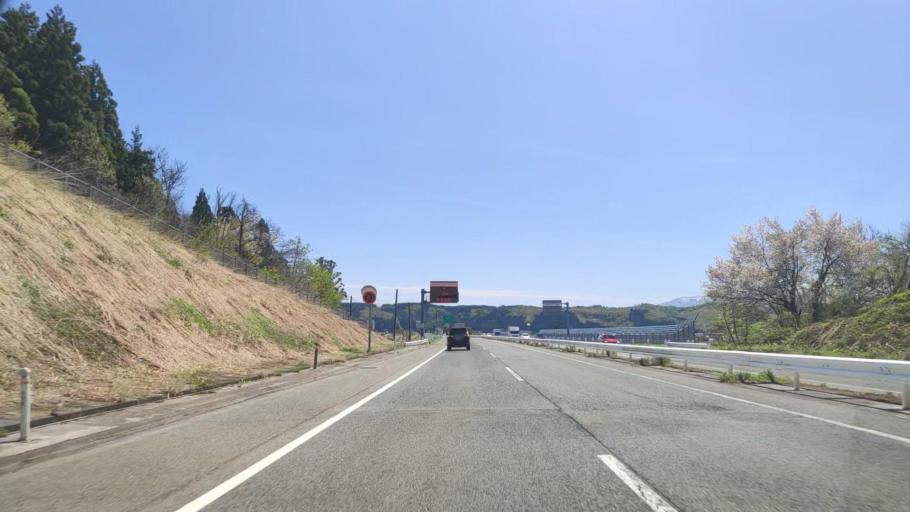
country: JP
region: Yamagata
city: Shinjo
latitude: 38.7091
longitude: 140.3087
